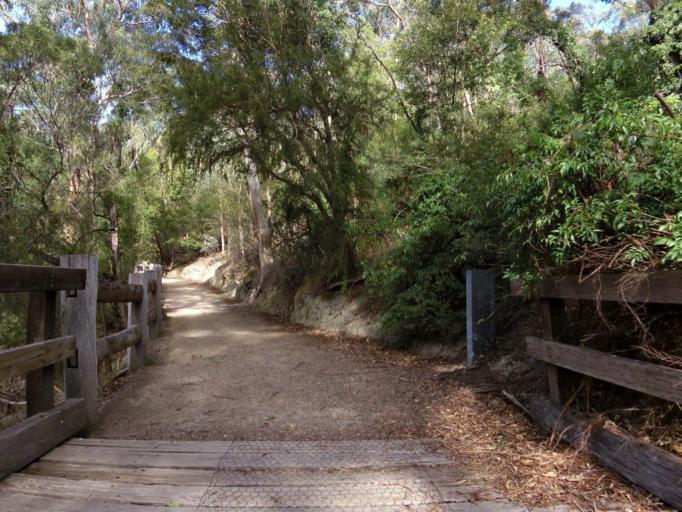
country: AU
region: Victoria
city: Mitcham
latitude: -37.8072
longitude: 145.2052
